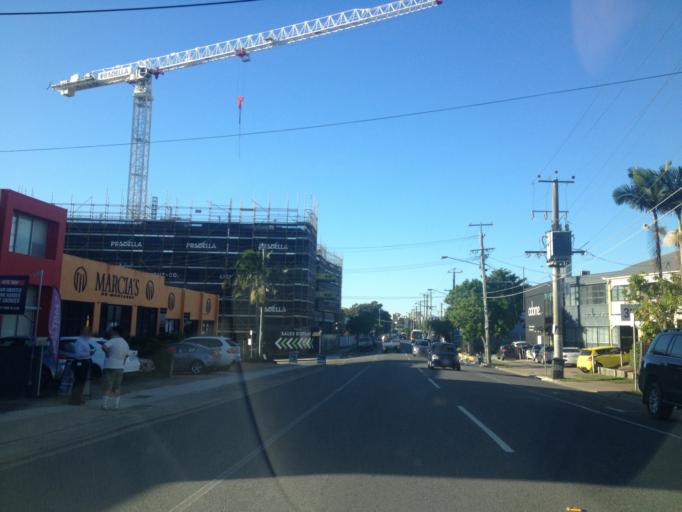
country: AU
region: Queensland
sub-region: Brisbane
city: Milton
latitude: -27.4822
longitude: 153.0039
